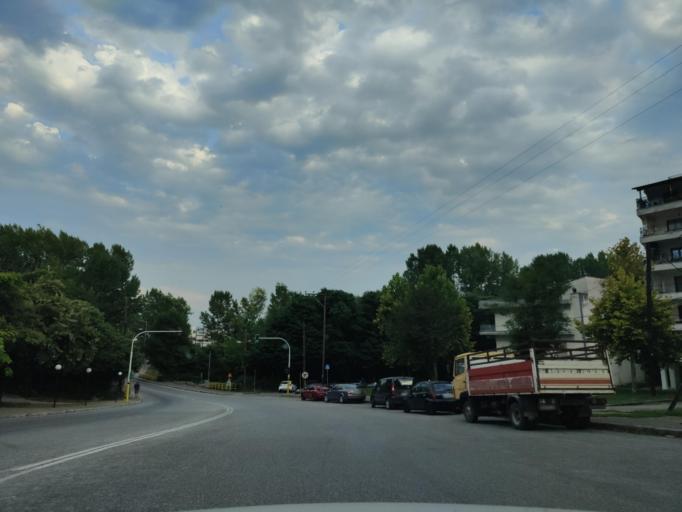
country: GR
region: East Macedonia and Thrace
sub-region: Nomos Dramas
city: Drama
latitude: 41.1491
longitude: 24.1395
